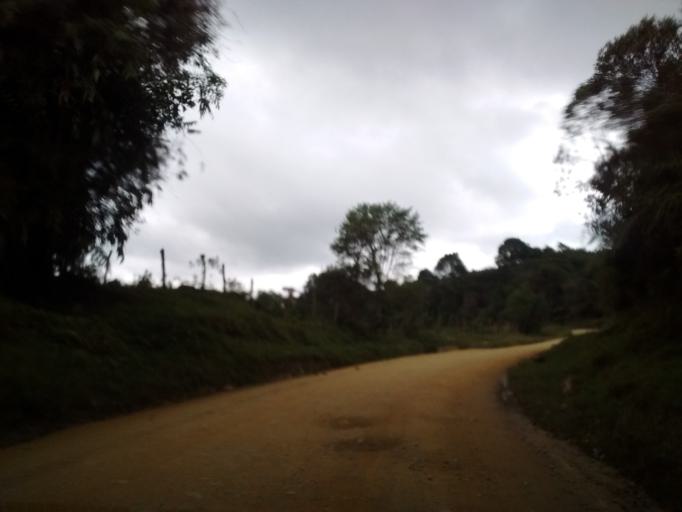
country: CO
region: Huila
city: Isnos
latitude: 2.0271
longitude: -76.2726
